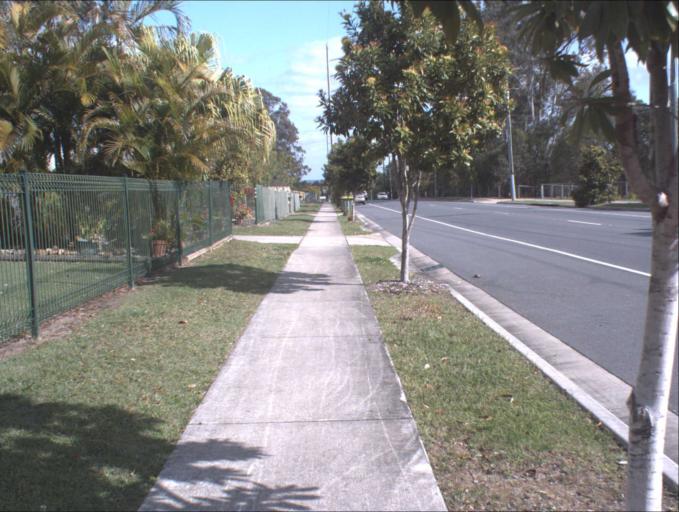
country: AU
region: Queensland
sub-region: Logan
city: Waterford West
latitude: -27.6894
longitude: 153.1200
